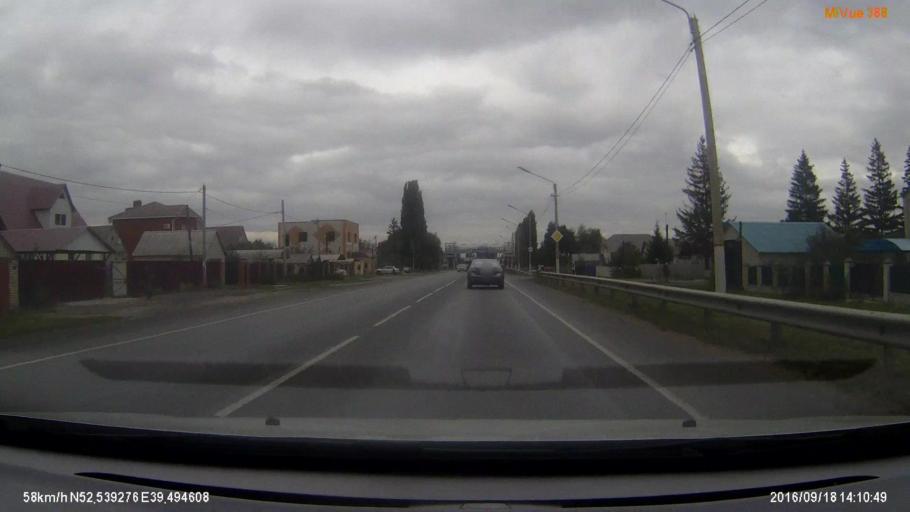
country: RU
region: Lipetsk
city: Syrskoye
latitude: 52.5923
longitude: 39.5162
